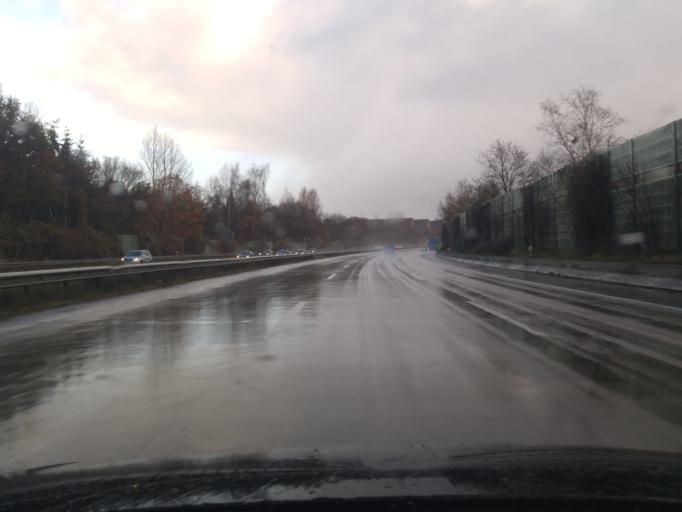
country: DE
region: Schleswig-Holstein
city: Stockelsdorf
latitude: 53.8935
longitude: 10.6714
